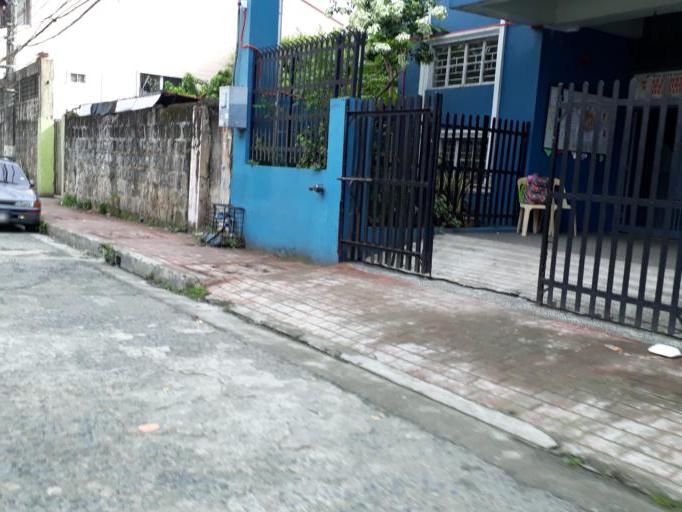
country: PH
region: Calabarzon
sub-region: Province of Rizal
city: Valenzuela
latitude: 14.6758
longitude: 120.9883
